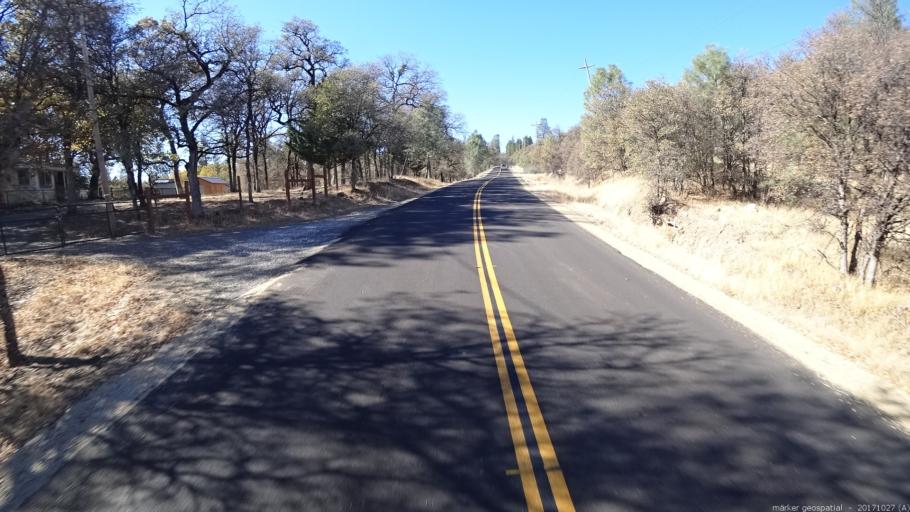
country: US
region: California
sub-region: Shasta County
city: Shingletown
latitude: 40.6794
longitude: -121.8776
